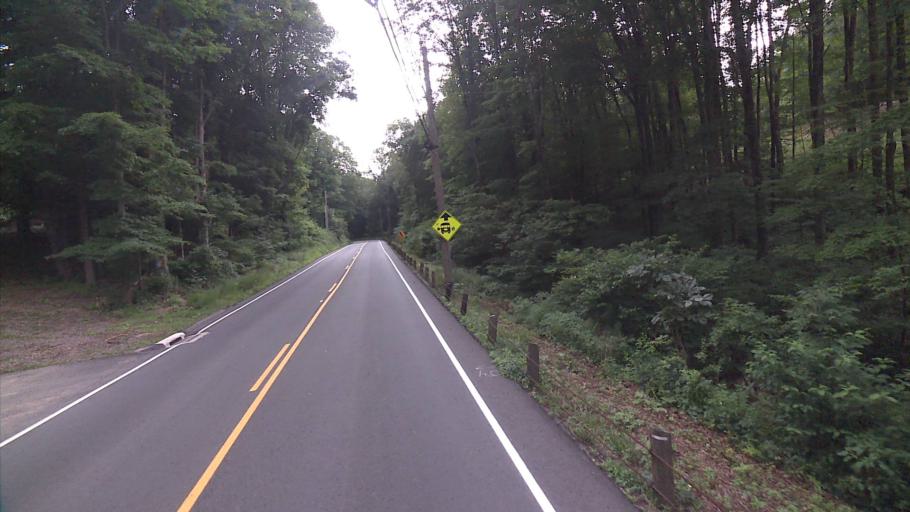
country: US
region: Connecticut
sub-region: New Haven County
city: Heritage Village
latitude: 41.5185
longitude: -73.2619
